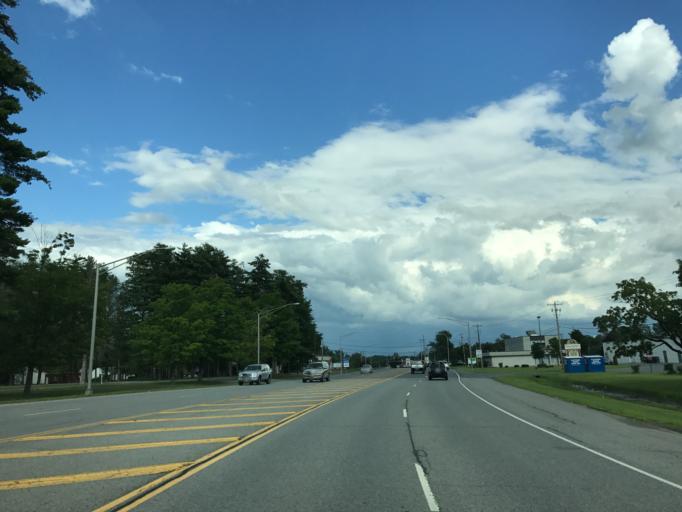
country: US
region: New York
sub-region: Warren County
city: Glens Falls North
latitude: 43.3312
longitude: -73.6713
